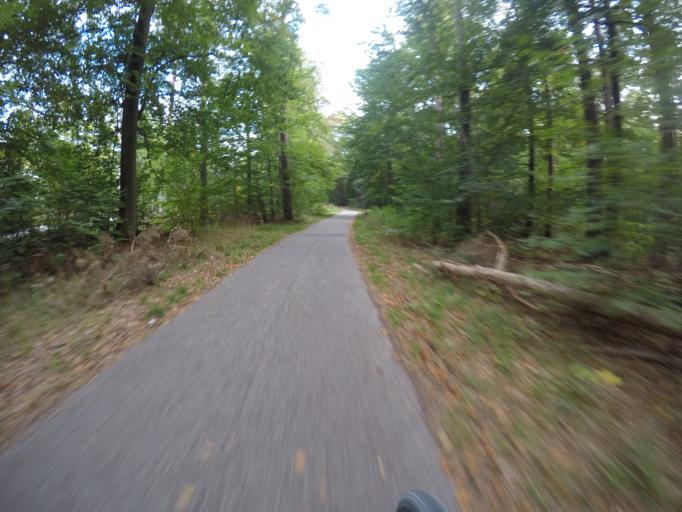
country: DE
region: Baden-Wuerttemberg
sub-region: Regierungsbezirk Stuttgart
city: Sindelfingen
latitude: 48.6919
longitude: 9.0396
